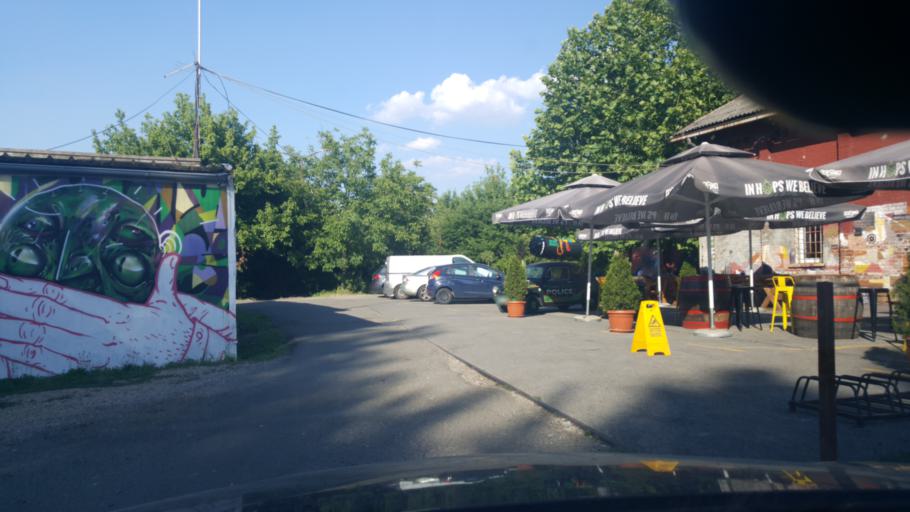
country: RS
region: Central Serbia
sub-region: Belgrade
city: Cukarica
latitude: 44.7887
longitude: 20.4228
